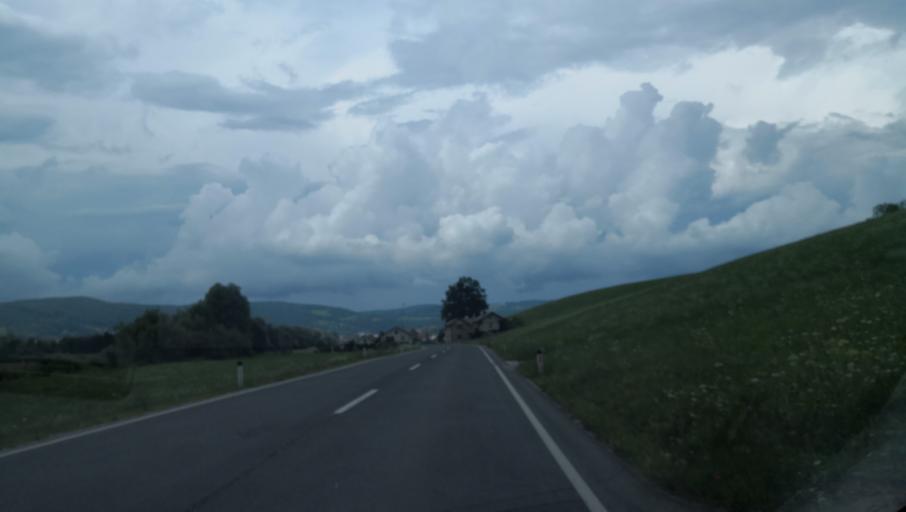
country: SI
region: Ivancna Gorica
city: Ivancna Gorica
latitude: 45.9237
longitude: 14.8048
